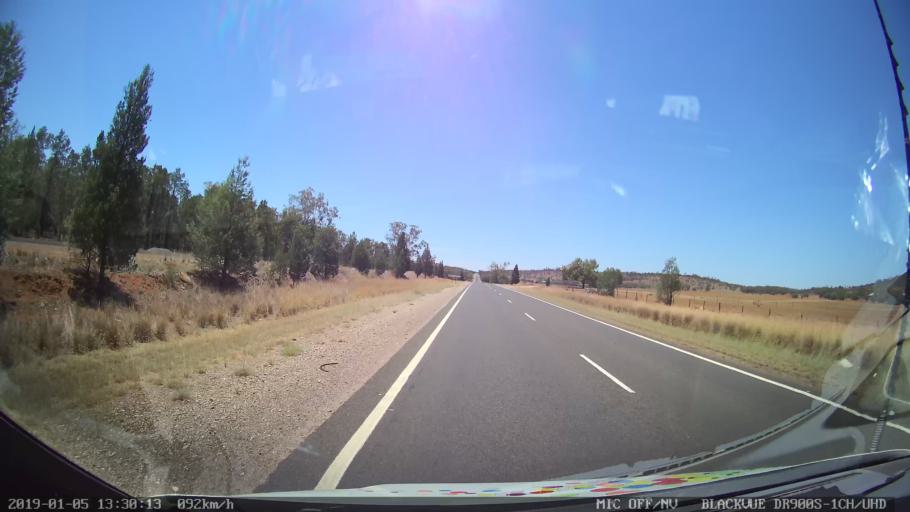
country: AU
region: New South Wales
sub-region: Gunnedah
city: Gunnedah
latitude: -31.0208
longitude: 150.0677
